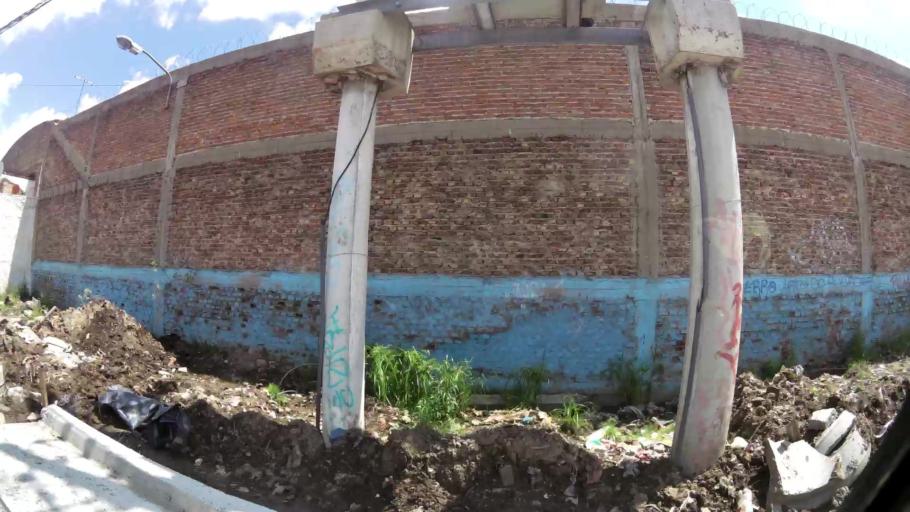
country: AR
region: Buenos Aires F.D.
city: Villa Lugano
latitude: -34.6876
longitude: -58.4415
